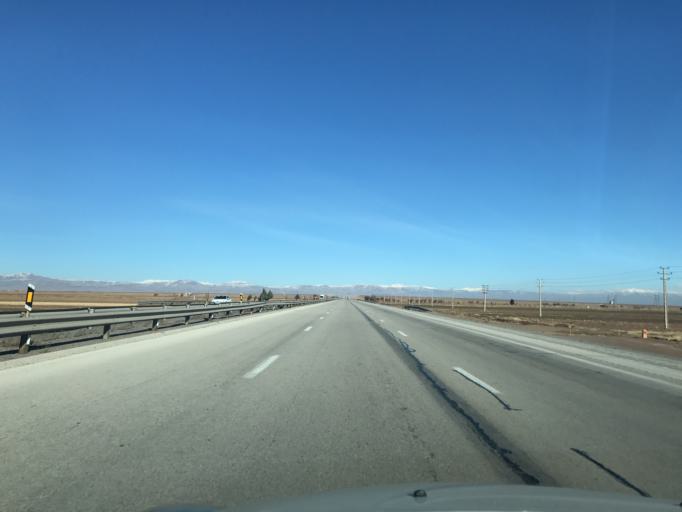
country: IR
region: Qazvin
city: Takestan
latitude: 36.1660
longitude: 49.7962
